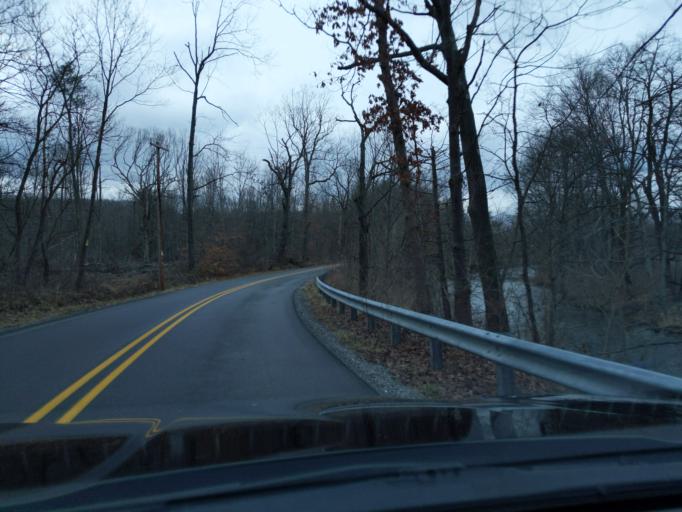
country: US
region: Pennsylvania
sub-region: Blair County
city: Bellwood
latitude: 40.6250
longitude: -78.3189
